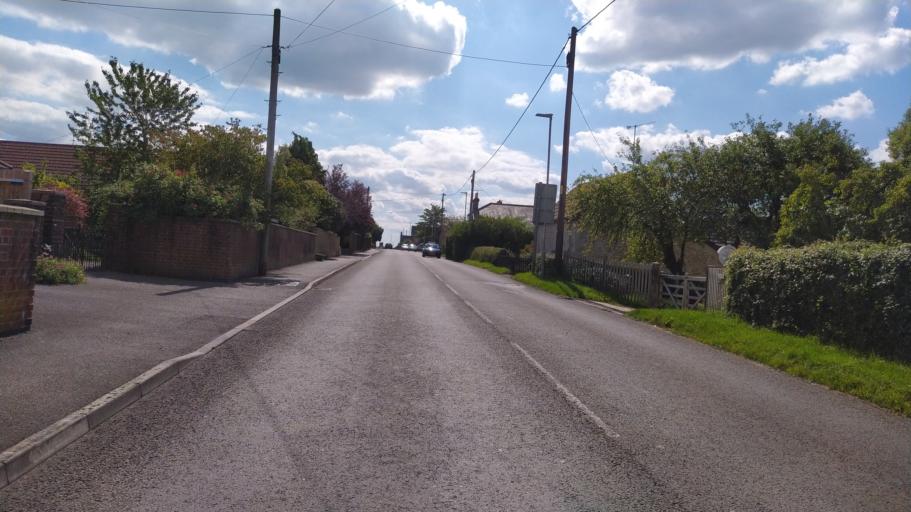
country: GB
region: England
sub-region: Dorset
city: Gillingham
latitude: 51.0480
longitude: -2.2807
